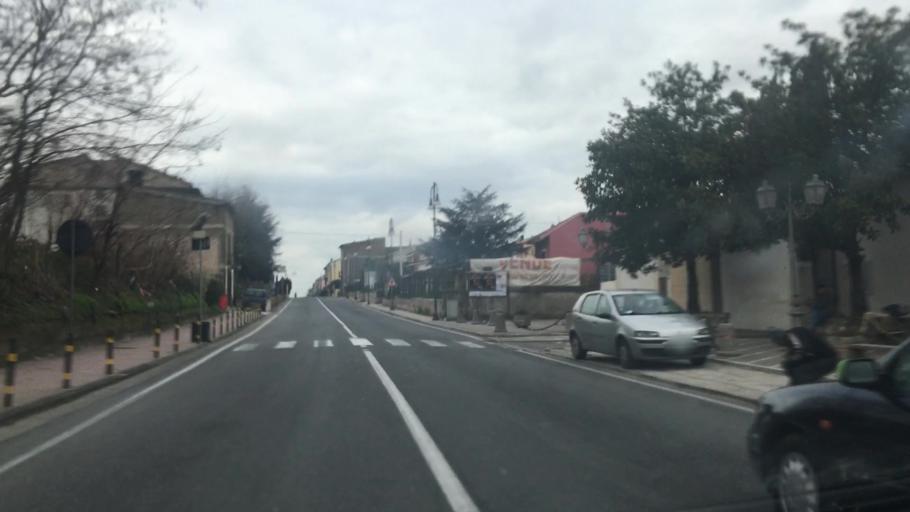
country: IT
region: Campania
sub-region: Provincia di Benevento
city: Arpaia
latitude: 41.0384
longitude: 14.5532
